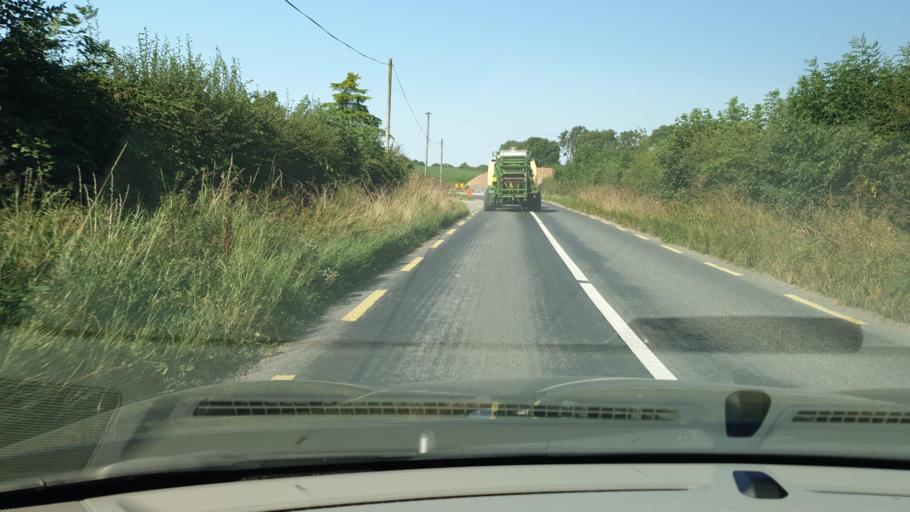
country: IE
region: Leinster
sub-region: An Mhi
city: Athboy
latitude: 53.5890
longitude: -6.8579
